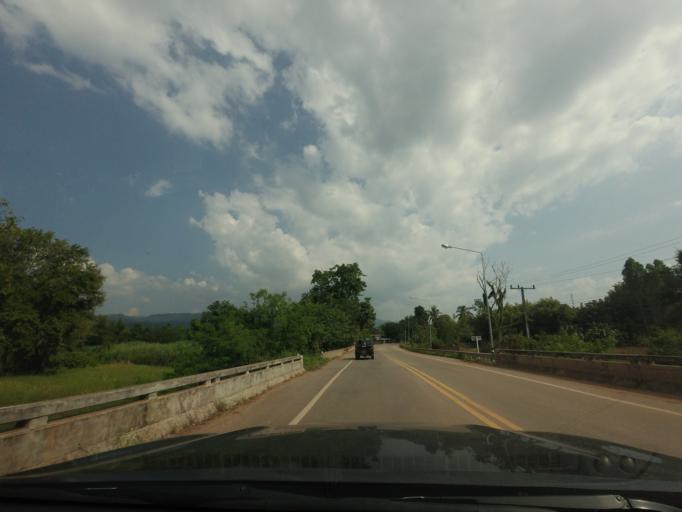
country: TH
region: Phitsanulok
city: Nakhon Thai
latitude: 17.0371
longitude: 100.9132
